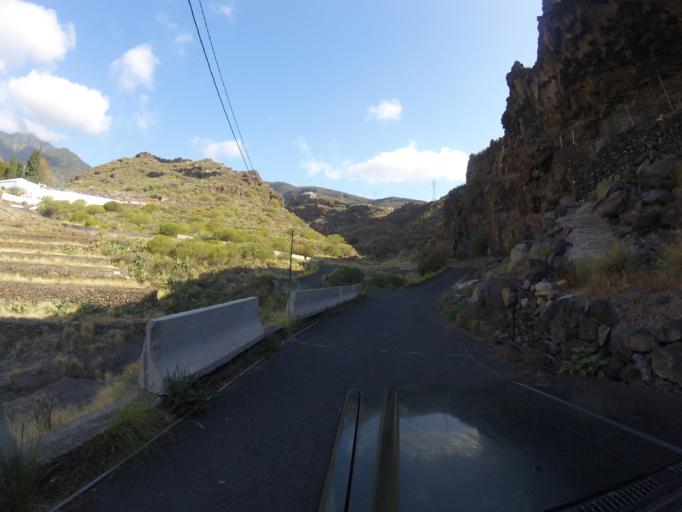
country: ES
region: Canary Islands
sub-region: Provincia de Santa Cruz de Tenerife
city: Candelaria
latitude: 28.3787
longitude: -16.3744
